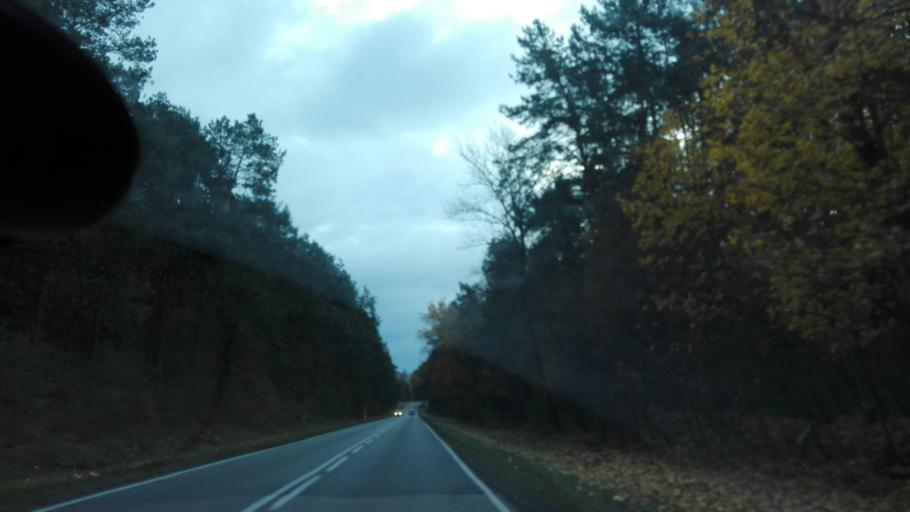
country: PL
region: Lublin Voivodeship
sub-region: Powiat pulawski
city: Pulawy
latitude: 51.4462
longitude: 21.9013
